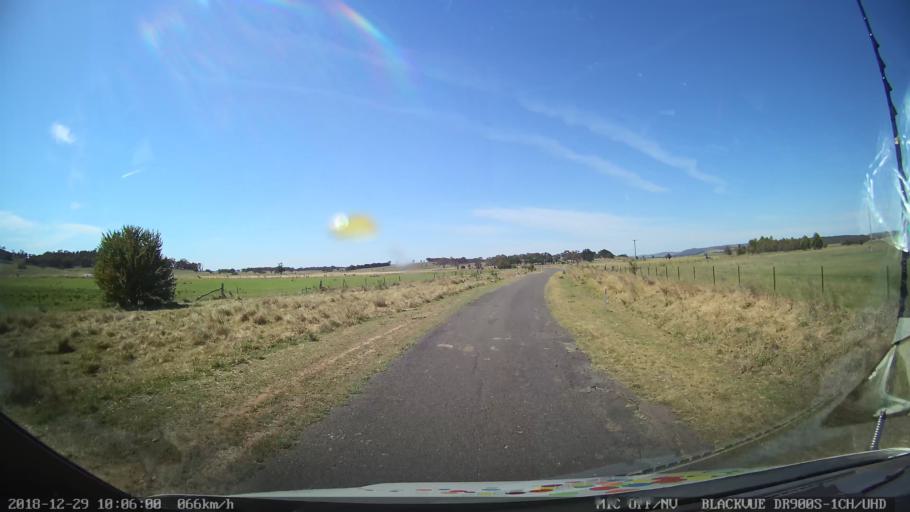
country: AU
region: New South Wales
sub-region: Goulburn Mulwaree
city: Goulburn
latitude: -34.8389
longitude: 149.4543
